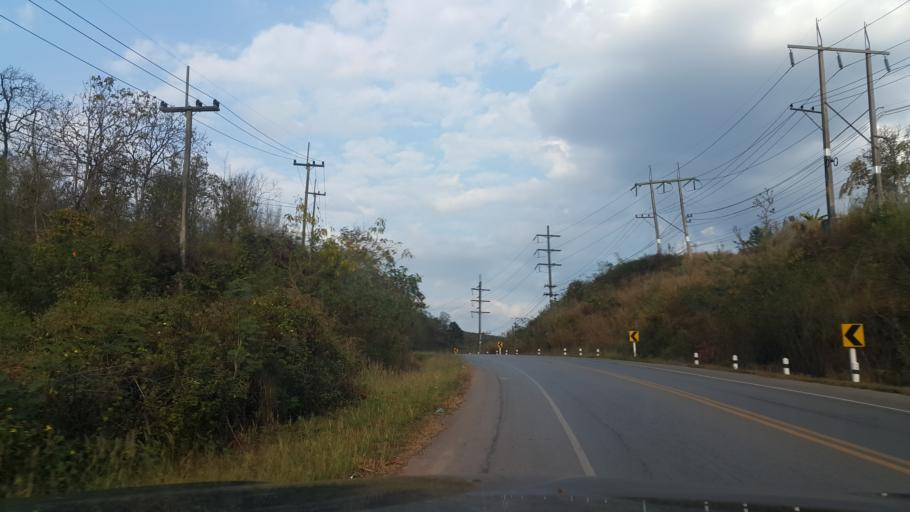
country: TH
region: Loei
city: Dan Sai
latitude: 17.3119
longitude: 101.2082
